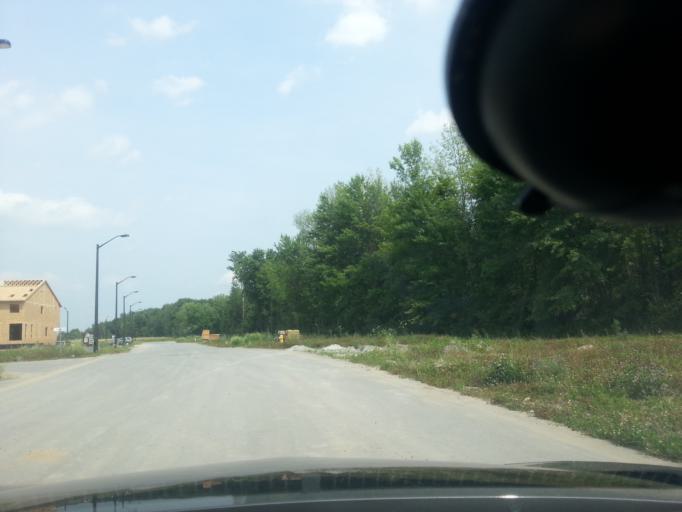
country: CA
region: Ontario
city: Bells Corners
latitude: 45.2635
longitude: -75.6956
